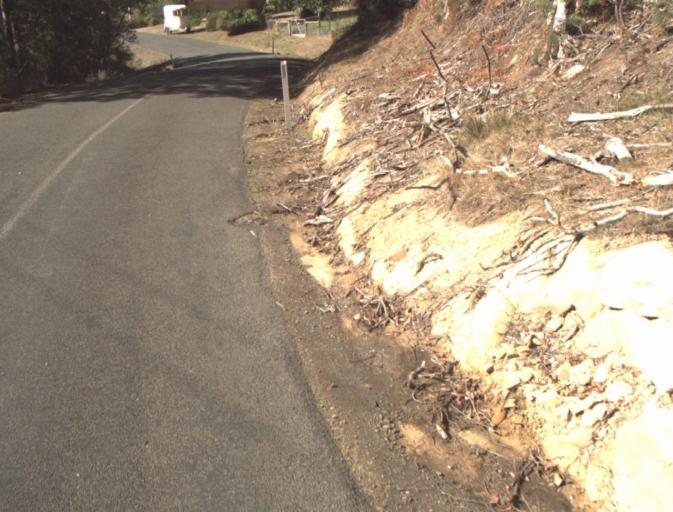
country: AU
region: Tasmania
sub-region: Launceston
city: Mayfield
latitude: -41.2954
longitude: 147.2025
